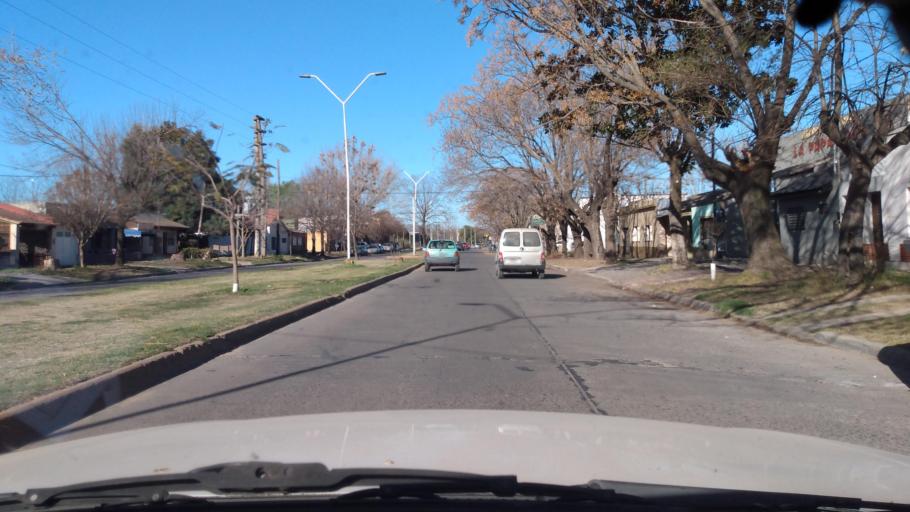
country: AR
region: Buenos Aires
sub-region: Partido de Mercedes
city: Mercedes
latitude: -34.6464
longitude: -59.4201
